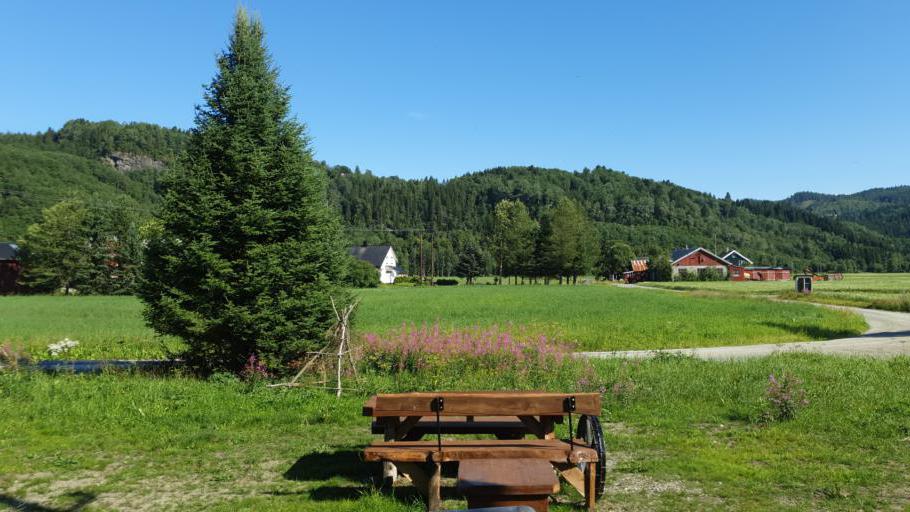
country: NO
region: Sor-Trondelag
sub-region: Orkdal
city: Orkanger
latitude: 63.2067
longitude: 9.7854
